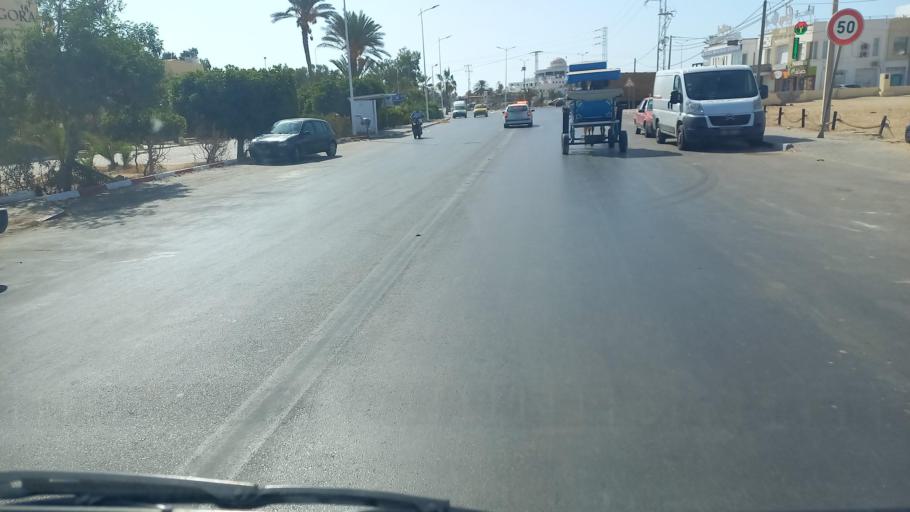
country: TN
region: Madanin
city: Midoun
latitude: 33.8399
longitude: 10.9920
